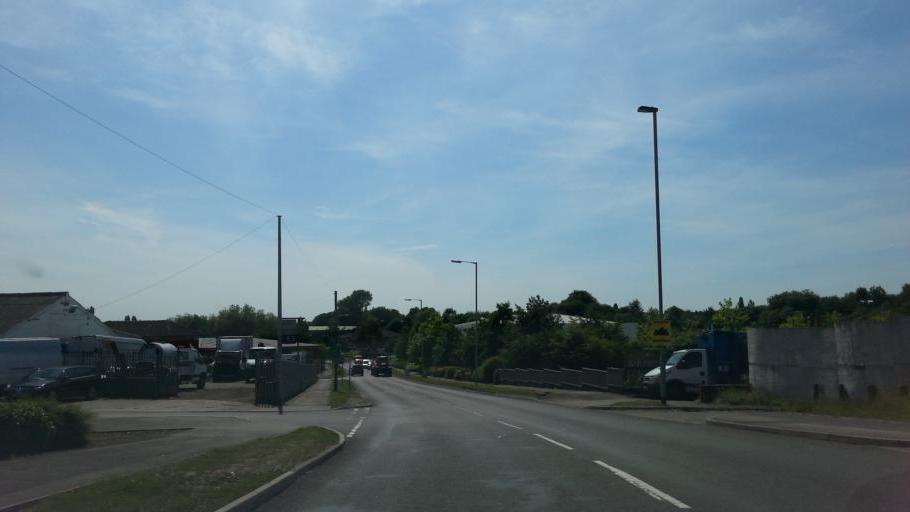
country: GB
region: England
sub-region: Staffordshire
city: Cannock
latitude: 52.7003
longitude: -2.0064
